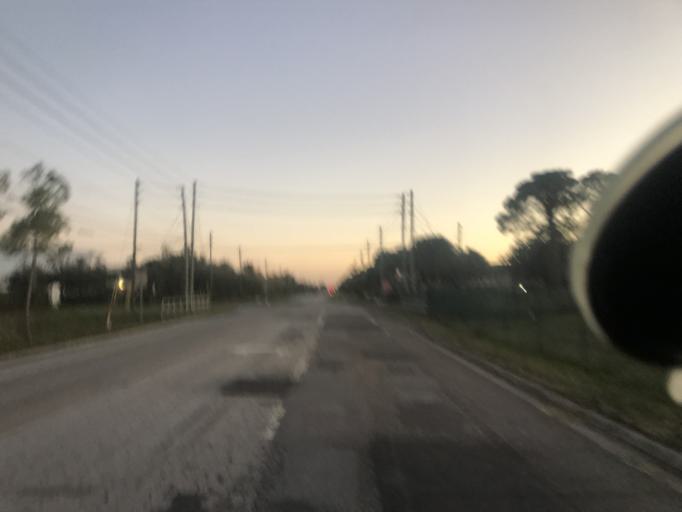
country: US
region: Florida
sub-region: Pinellas County
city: Gandy
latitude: 27.8653
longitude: -82.6553
